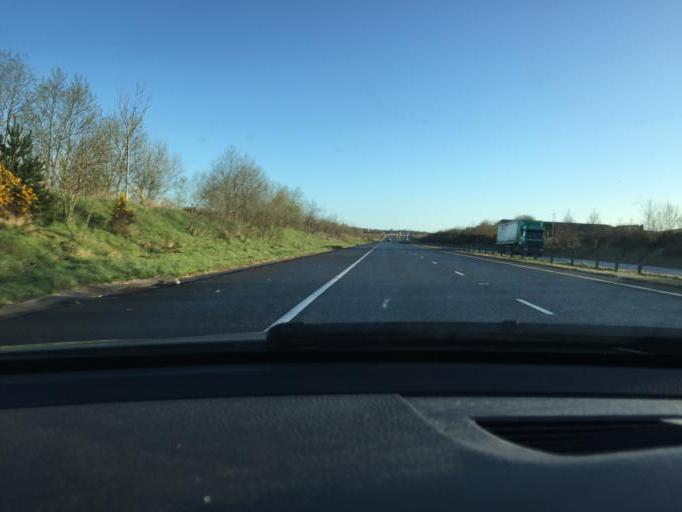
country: GB
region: Northern Ireland
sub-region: Newry and Mourne District
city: Newry
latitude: 54.1202
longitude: -6.3618
